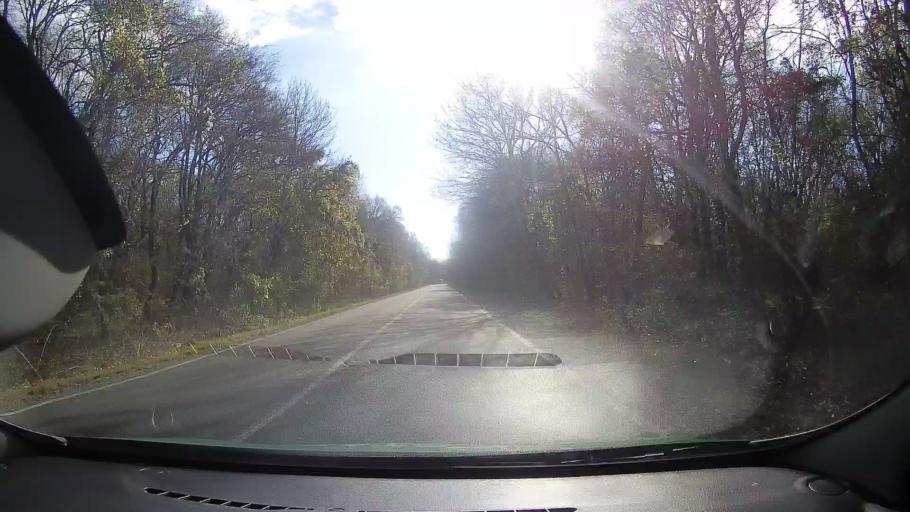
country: RO
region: Tulcea
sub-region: Oras Babadag
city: Babadag
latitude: 44.8482
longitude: 28.6986
